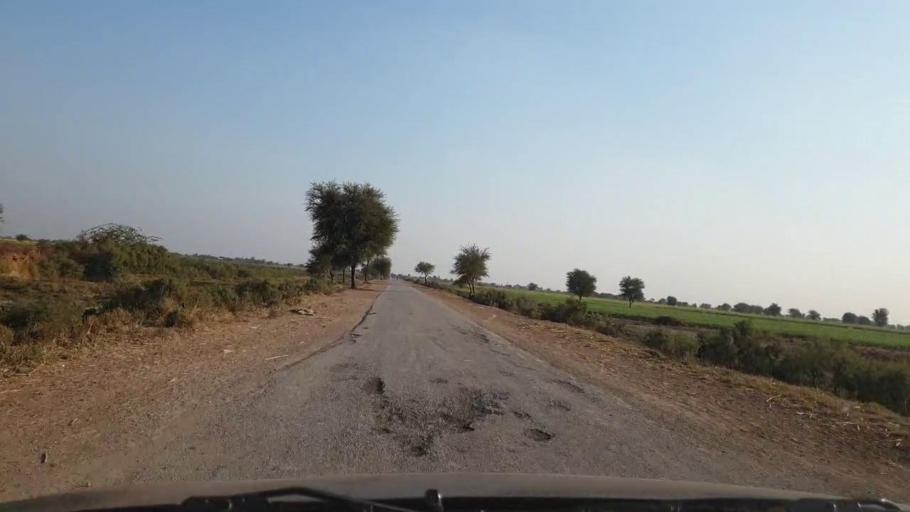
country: PK
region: Sindh
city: Jhol
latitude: 25.9397
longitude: 68.9108
